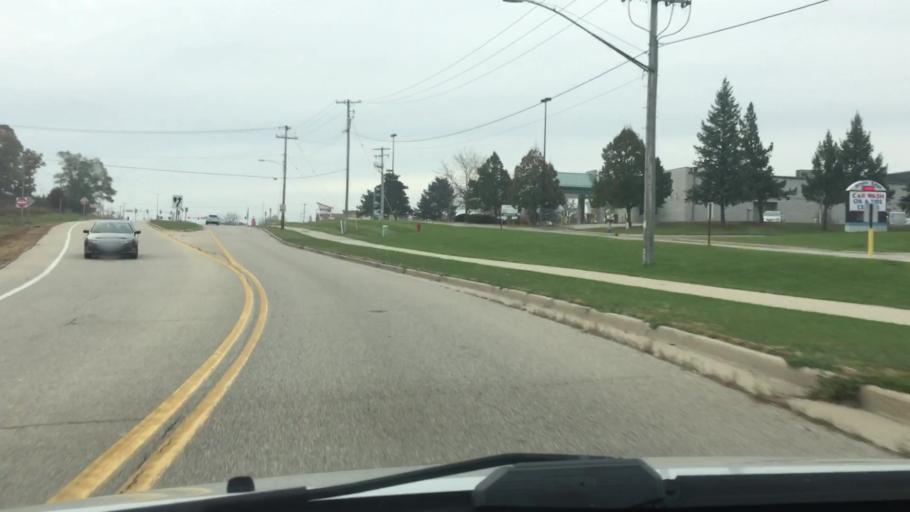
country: US
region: Wisconsin
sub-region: Waukesha County
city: Mukwonago
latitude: 42.8562
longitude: -88.3270
